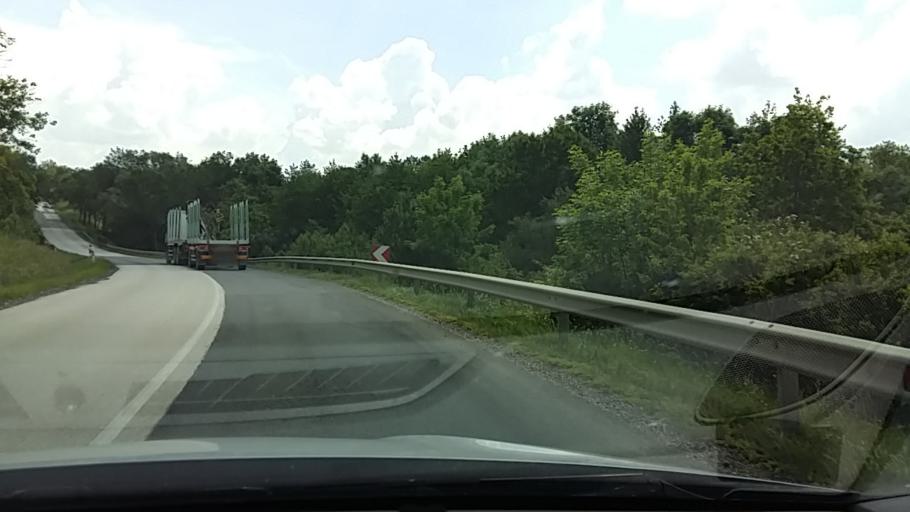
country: HU
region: Vas
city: Kormend
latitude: 46.9312
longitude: 16.6785
